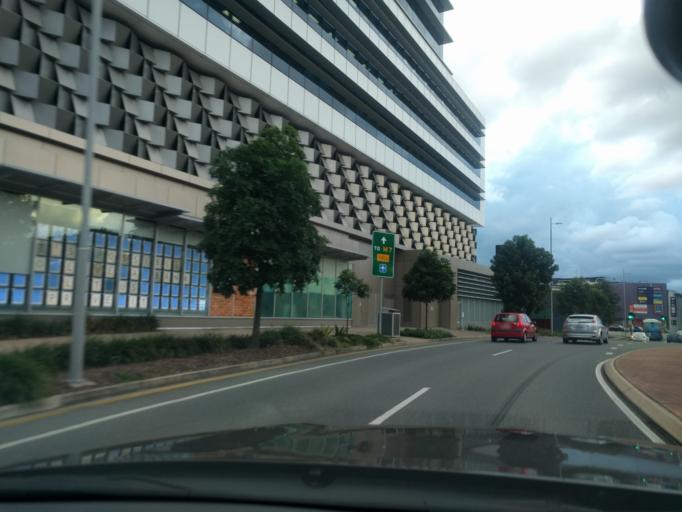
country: AU
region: Queensland
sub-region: Brisbane
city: Fortitude Valley
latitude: -27.4501
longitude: 153.0429
